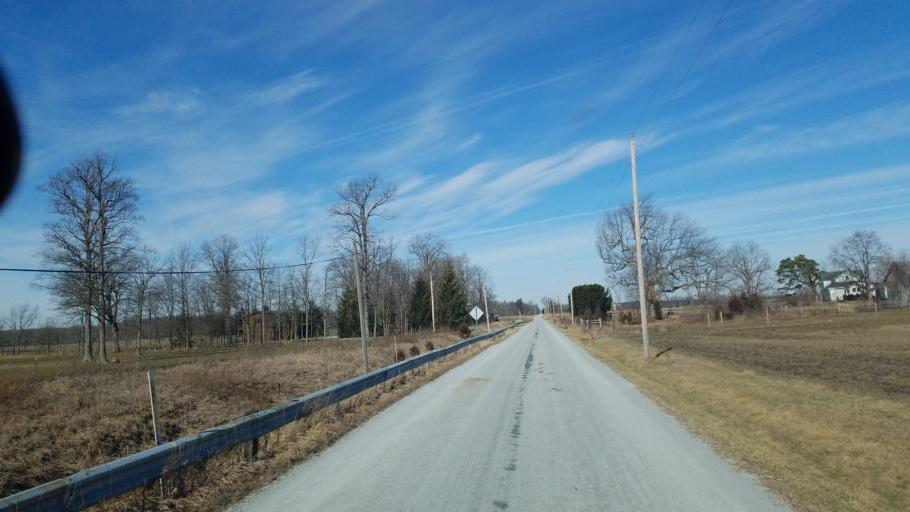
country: US
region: Ohio
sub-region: Hardin County
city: Kenton
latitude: 40.5887
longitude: -83.4747
